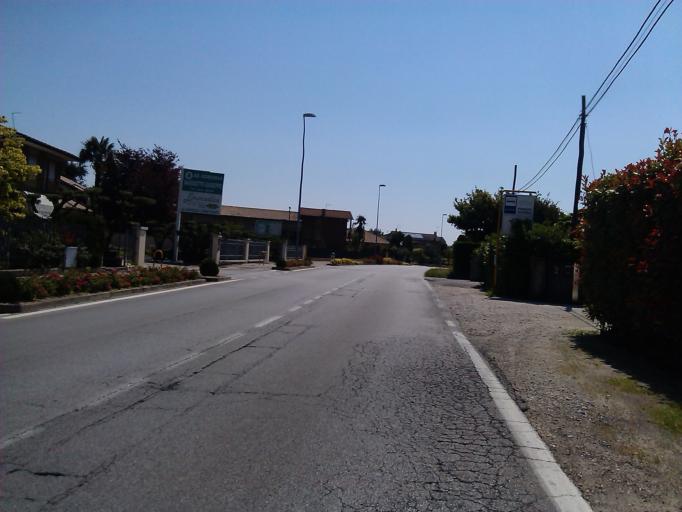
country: IT
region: Veneto
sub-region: Provincia di Treviso
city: Loria Bessica
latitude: 45.7350
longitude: 11.8515
